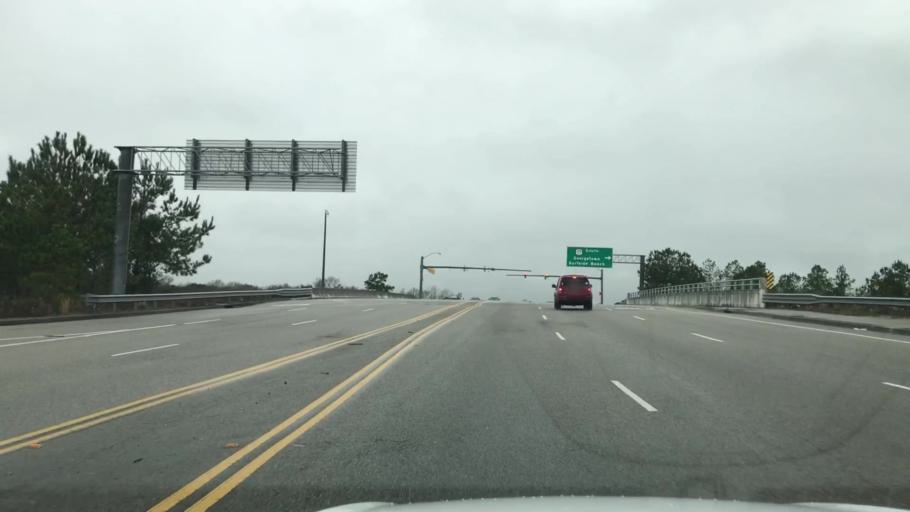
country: US
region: South Carolina
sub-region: Horry County
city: Forestbrook
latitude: 33.7031
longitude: -78.9302
